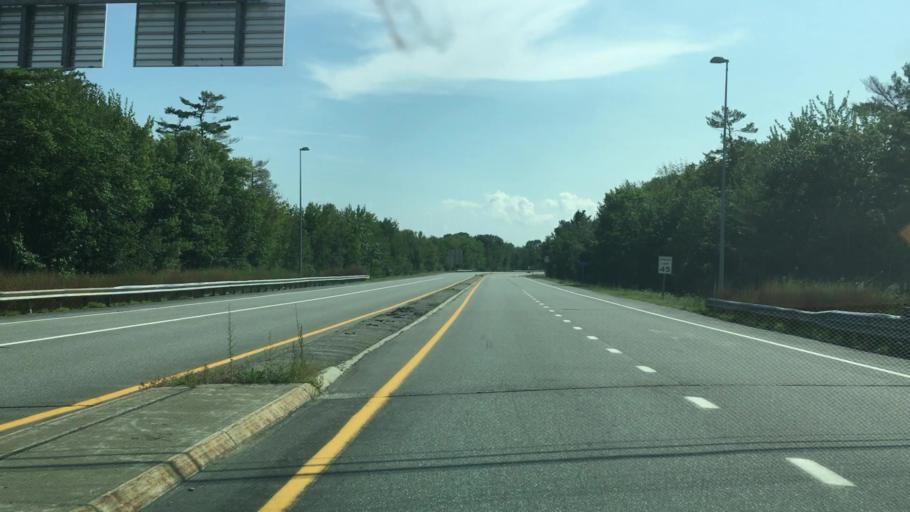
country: US
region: Maine
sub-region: Penobscot County
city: Bangor
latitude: 44.7841
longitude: -68.7948
